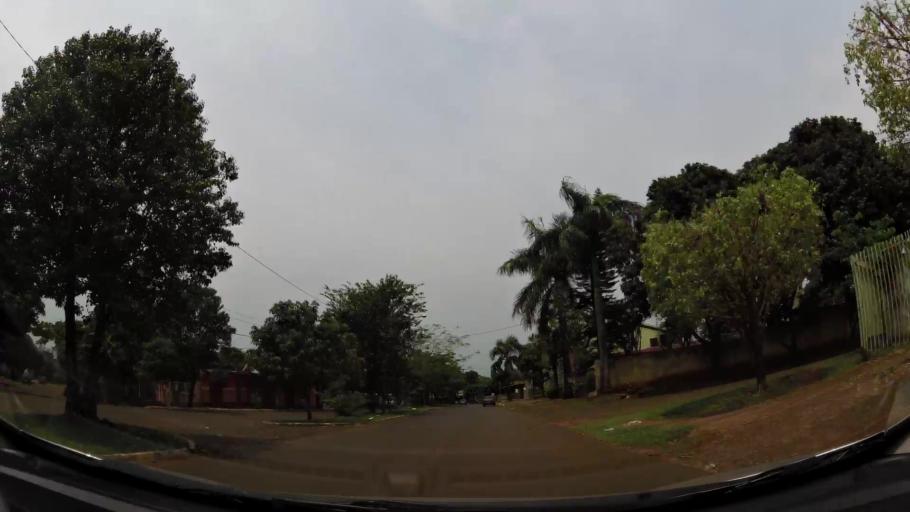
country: PY
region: Alto Parana
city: Presidente Franco
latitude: -25.5584
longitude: -54.6135
